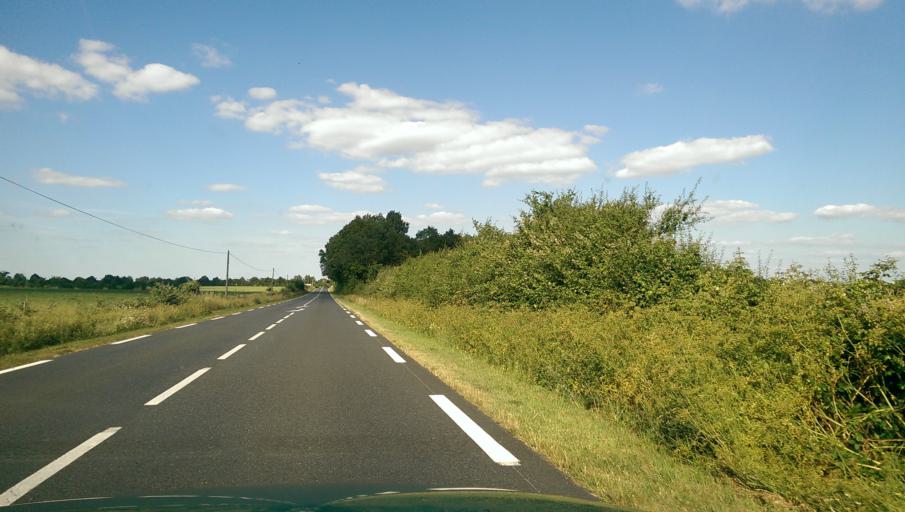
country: FR
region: Pays de la Loire
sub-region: Departement de la Loire-Atlantique
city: Vieillevigne
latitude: 46.9558
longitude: -1.4674
